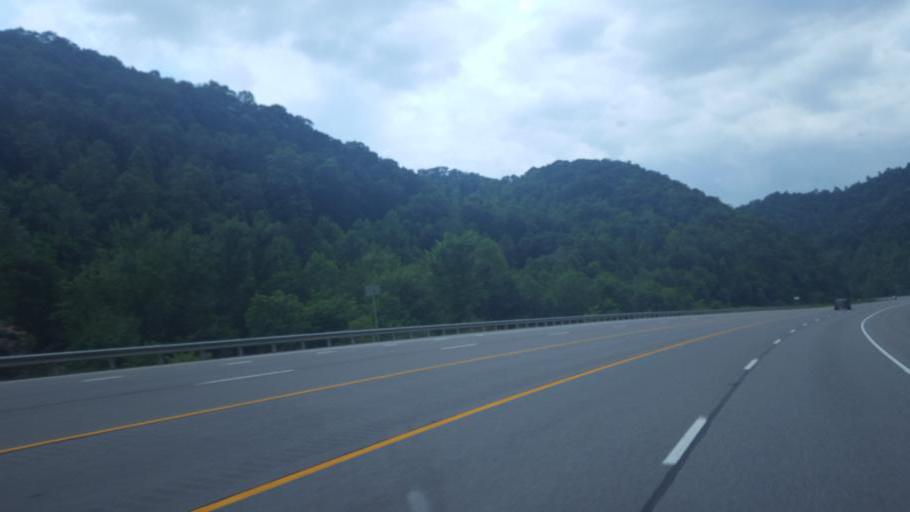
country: US
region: Kentucky
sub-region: Letcher County
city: Jenkins
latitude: 37.2530
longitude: -82.6155
